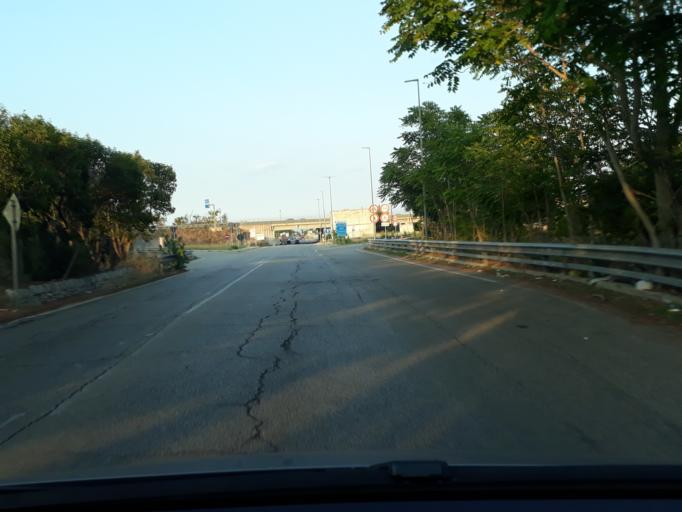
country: IT
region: Apulia
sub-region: Provincia di Brindisi
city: Fasano
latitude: 40.8392
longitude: 17.3699
